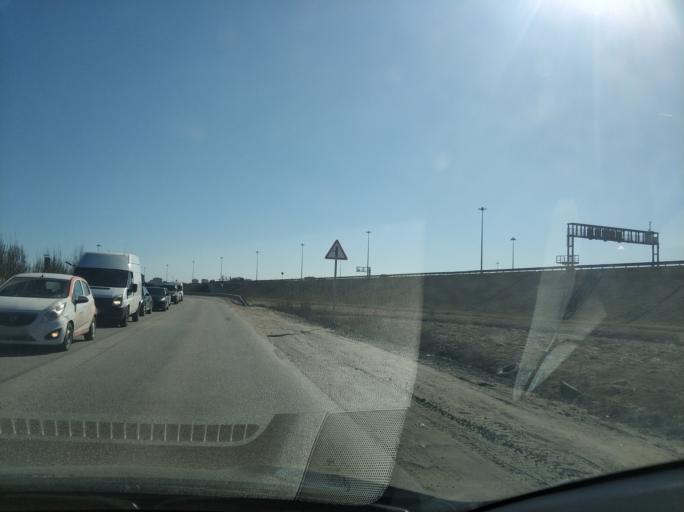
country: RU
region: Leningrad
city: Bugry
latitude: 60.0616
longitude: 30.3895
